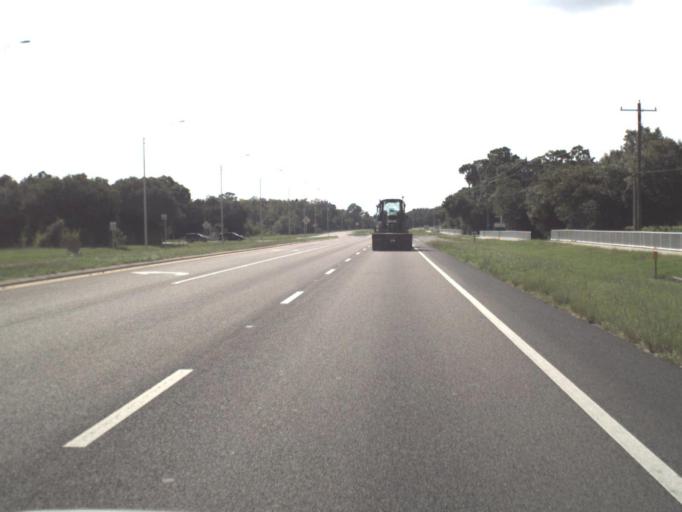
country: US
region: Florida
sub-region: Sarasota County
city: The Meadows
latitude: 27.4756
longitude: -82.3934
